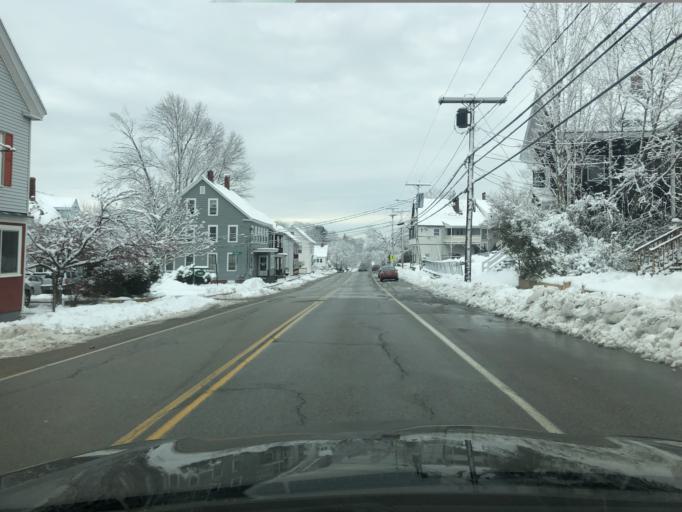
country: US
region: New Hampshire
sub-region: Strafford County
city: Somersworth
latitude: 43.2565
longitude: -70.8637
